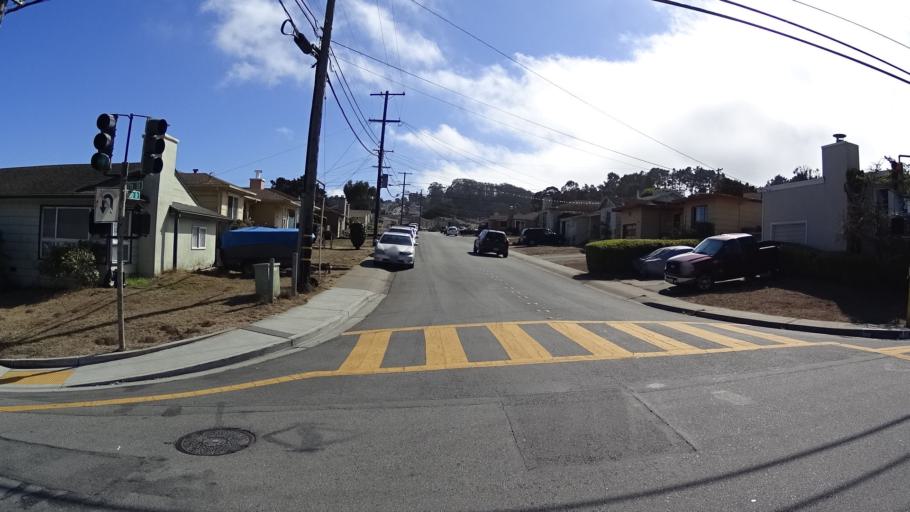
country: US
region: California
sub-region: San Mateo County
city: Broadmoor
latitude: 37.6932
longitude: -122.4802
